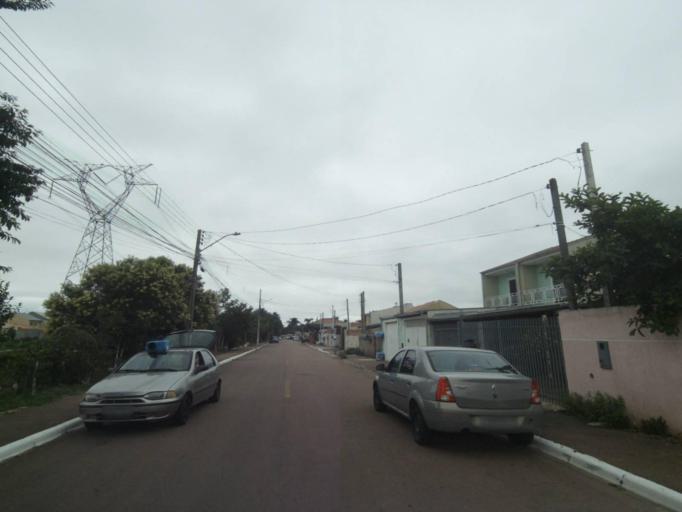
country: BR
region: Parana
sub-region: Araucaria
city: Araucaria
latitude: -25.5462
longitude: -49.3436
